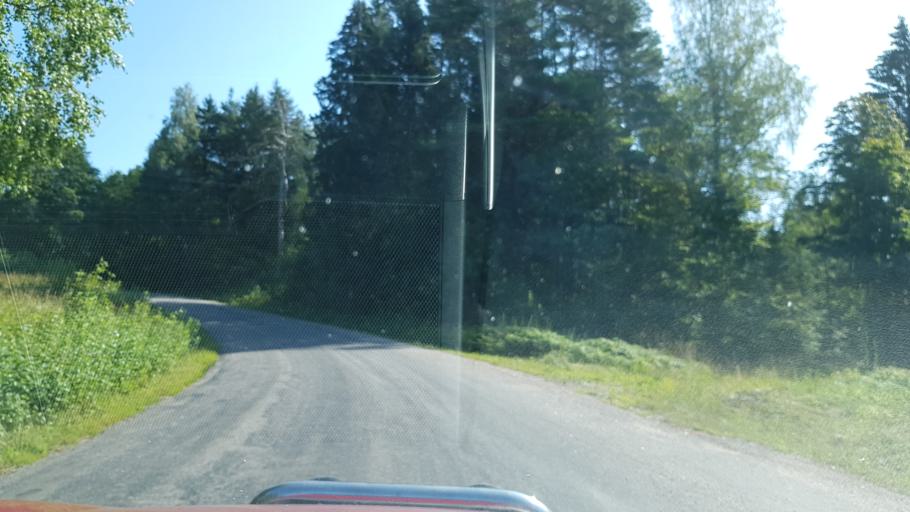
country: EE
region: Vorumaa
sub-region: Voru linn
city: Voru
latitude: 57.7174
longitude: 27.0834
